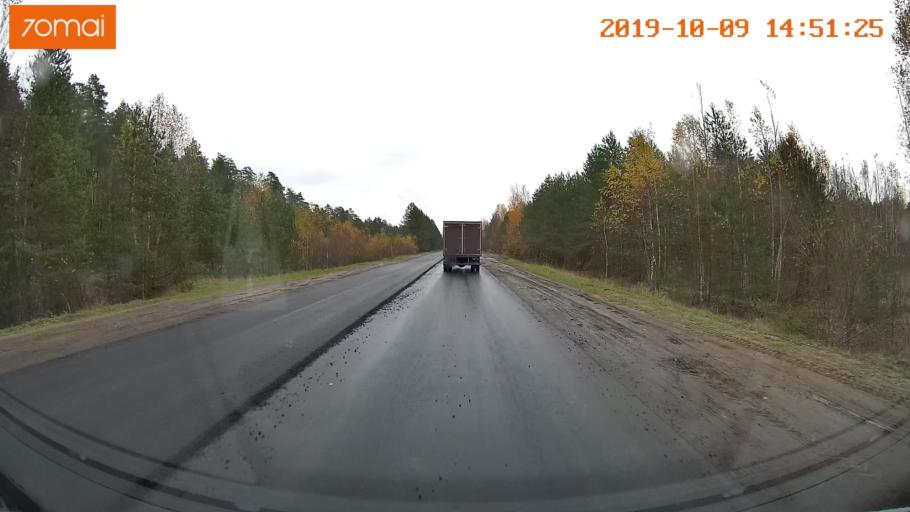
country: RU
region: Kostroma
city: Chistyye Bory
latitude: 58.3784
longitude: 41.6146
